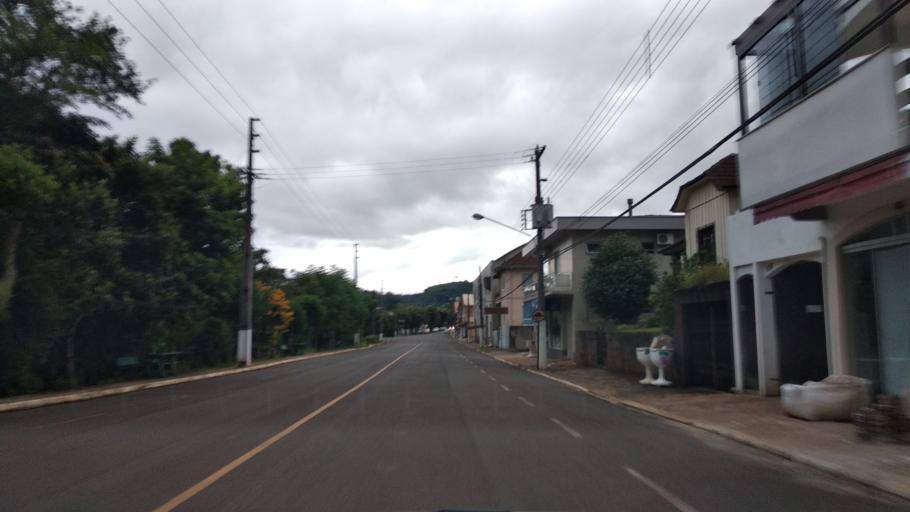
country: BR
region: Santa Catarina
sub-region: Videira
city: Videira
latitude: -27.0475
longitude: -51.2304
